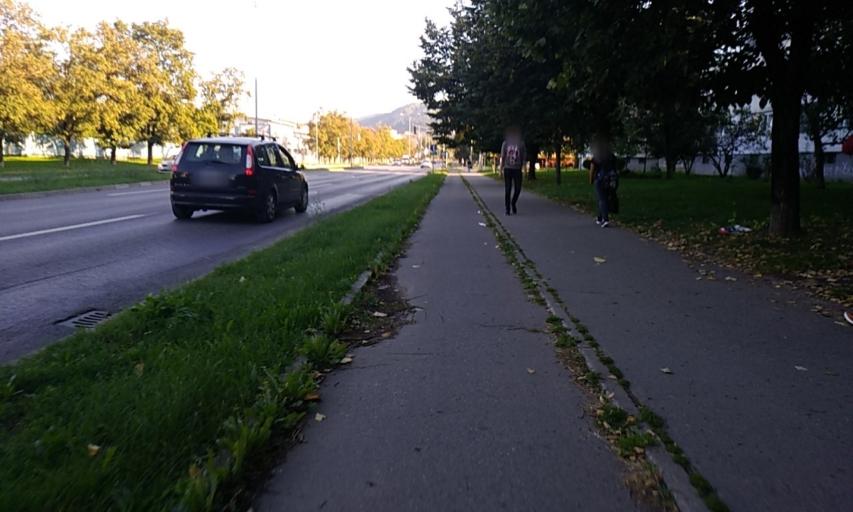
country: BA
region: Republika Srpska
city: Starcevica
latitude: 44.7730
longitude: 17.2084
